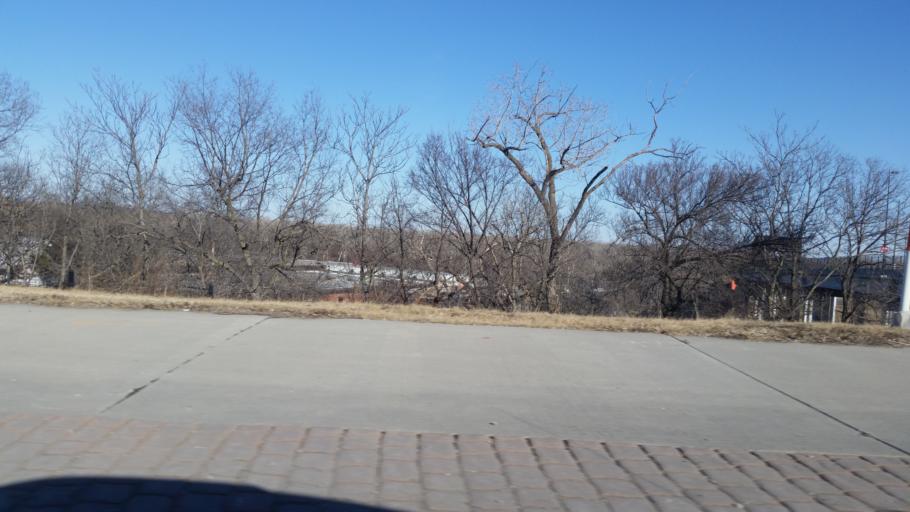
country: US
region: Nebraska
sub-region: Douglas County
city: Omaha
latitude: 41.2134
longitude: -95.9332
